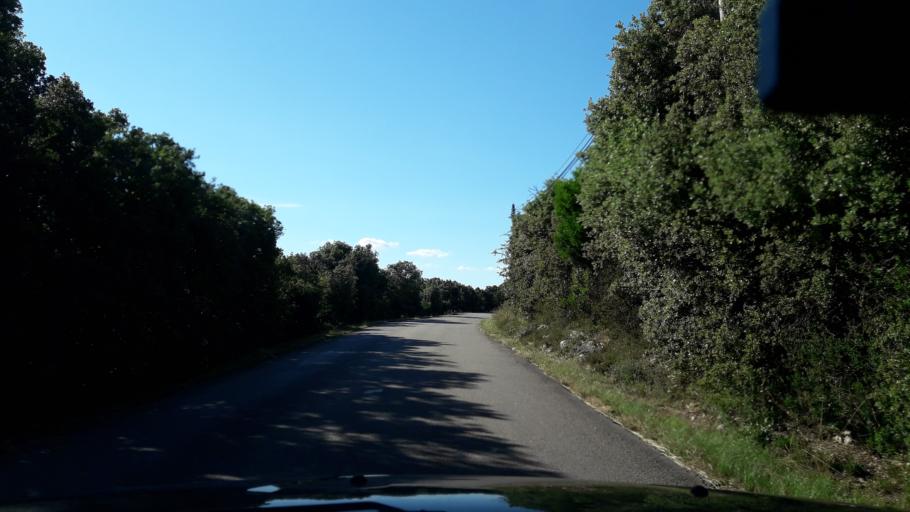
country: FR
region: Languedoc-Roussillon
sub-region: Departement du Gard
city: Saint-Julien-de-Peyrolas
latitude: 44.3739
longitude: 4.5055
